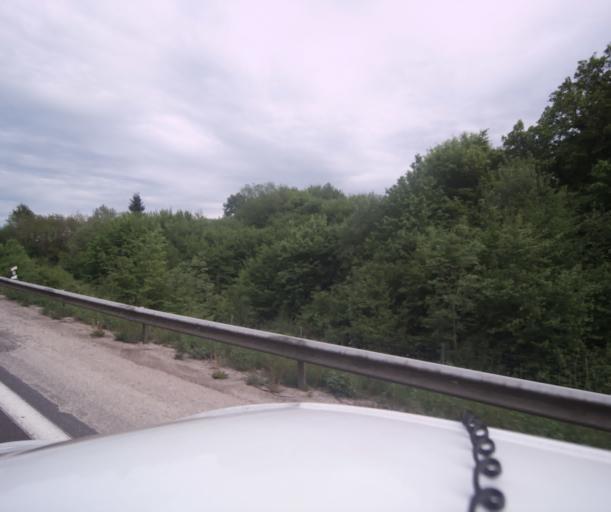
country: FR
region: Franche-Comte
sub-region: Departement du Doubs
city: Franois
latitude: 47.2171
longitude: 5.9189
